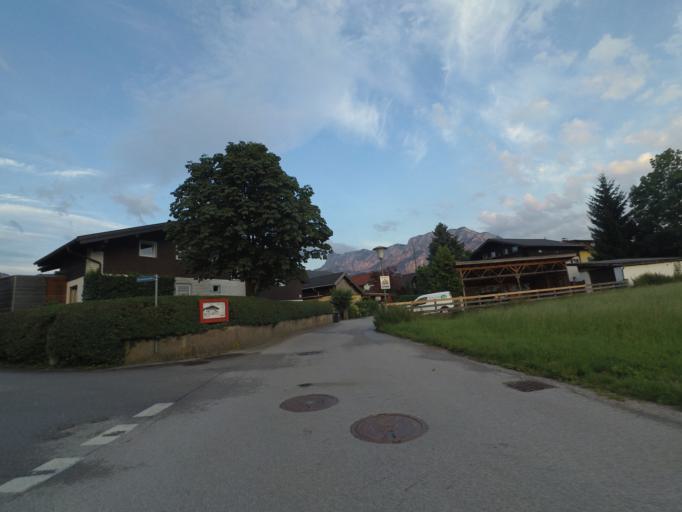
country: AT
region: Salzburg
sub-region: Politischer Bezirk Hallein
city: Puch bei Hallein
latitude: 47.7143
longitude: 13.0886
